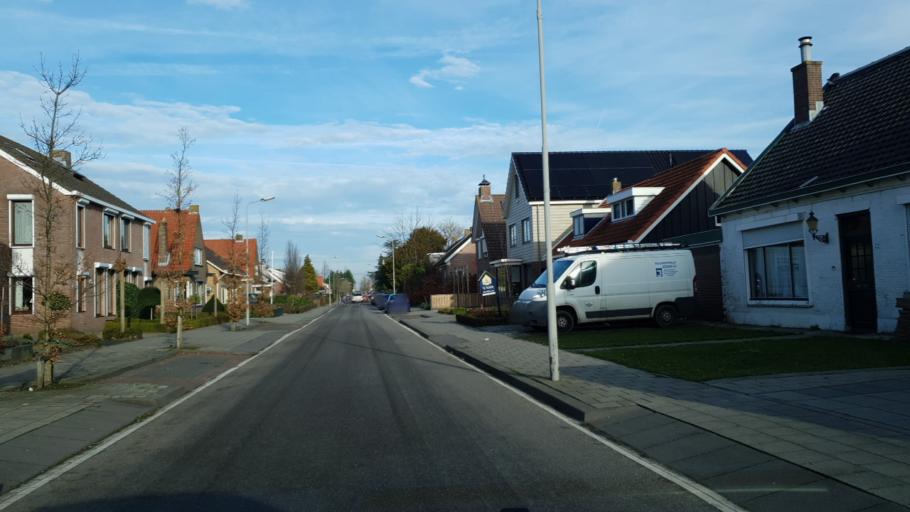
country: NL
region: Zeeland
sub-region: Gemeente Reimerswaal
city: Yerseke
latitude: 51.4320
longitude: 4.1127
